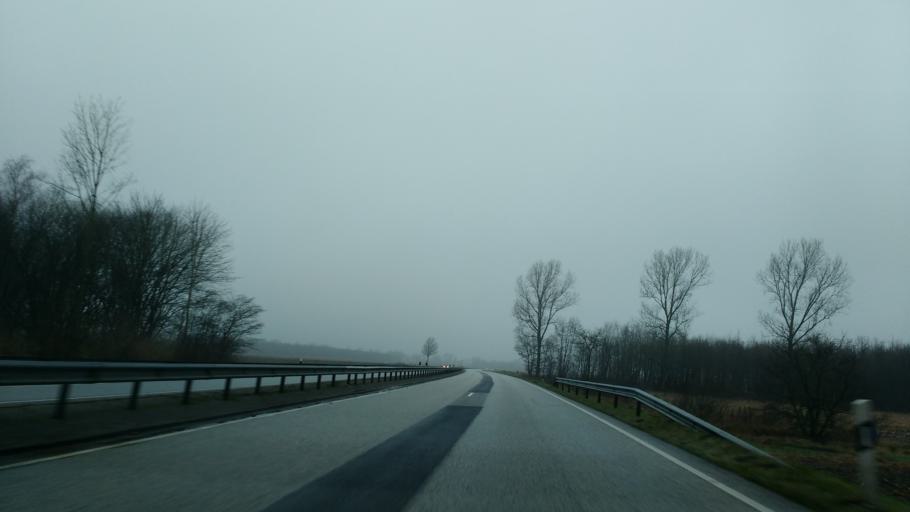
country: DE
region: Schleswig-Holstein
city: Jevenstedt
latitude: 54.2407
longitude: 9.6754
